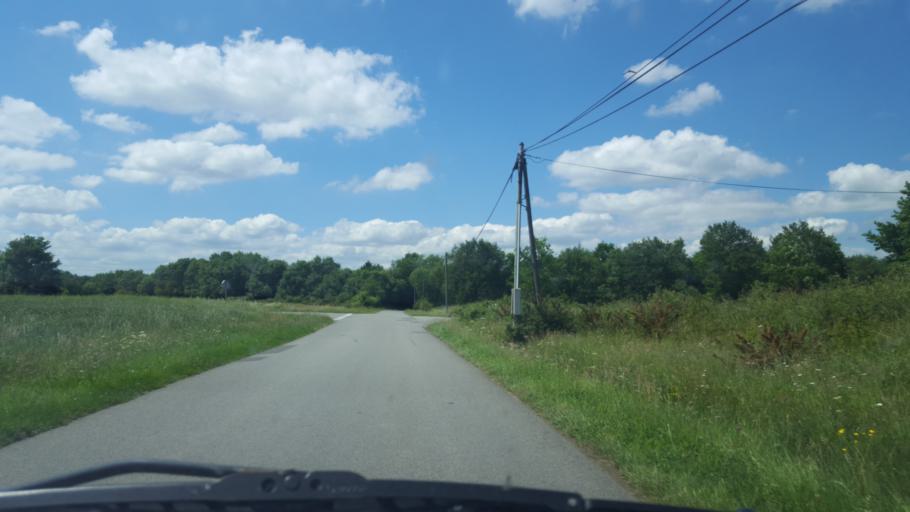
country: FR
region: Pays de la Loire
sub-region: Departement de la Loire-Atlantique
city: Saint-Philbert-de-Grand-Lieu
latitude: 47.0330
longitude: -1.6135
